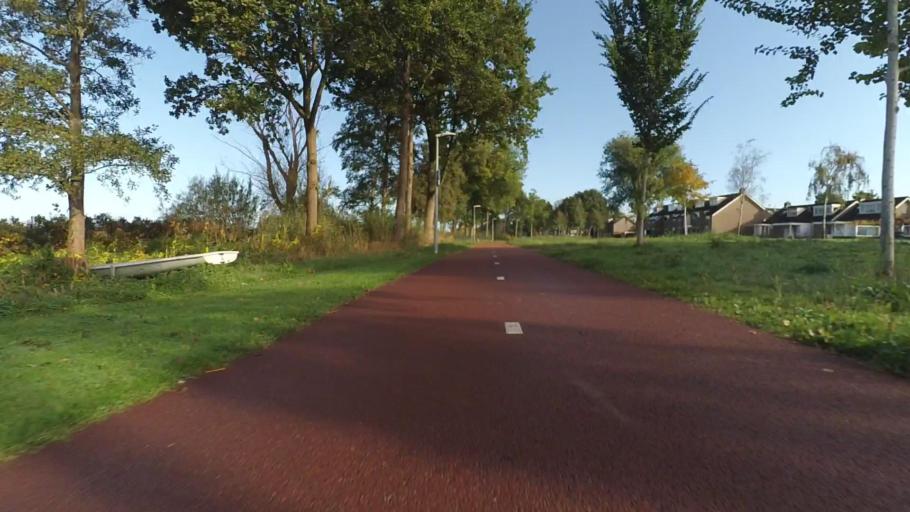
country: NL
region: Gelderland
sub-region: Gemeente Harderwijk
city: Harderwijk
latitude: 52.3372
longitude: 5.5995
